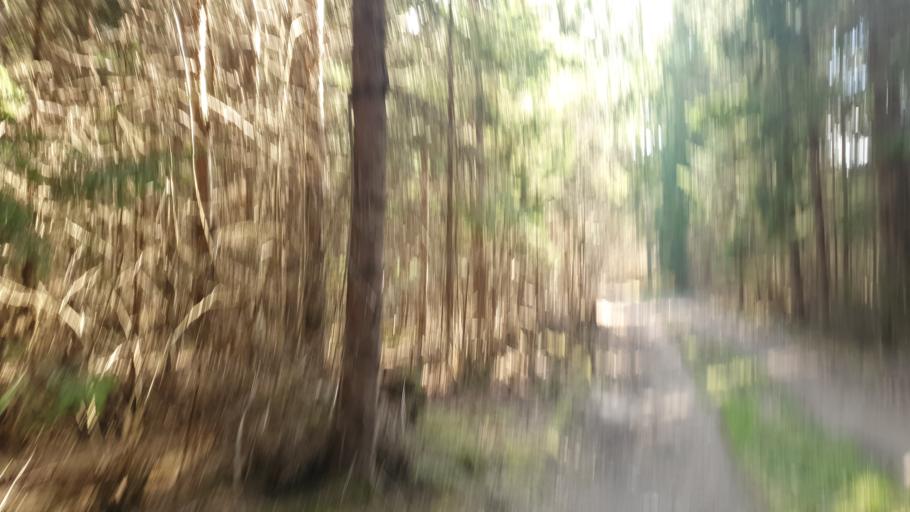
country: LT
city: Aukstadvaris
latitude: 54.4937
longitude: 24.6510
